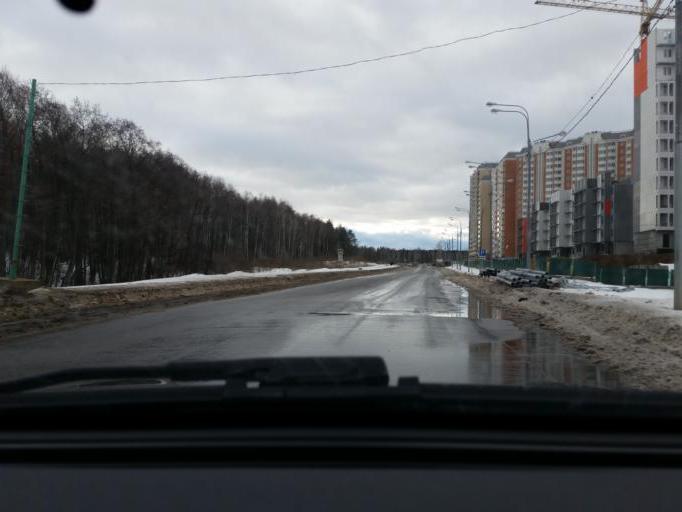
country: RU
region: Moskovskaya
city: Shcherbinka
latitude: 55.5251
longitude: 37.6004
